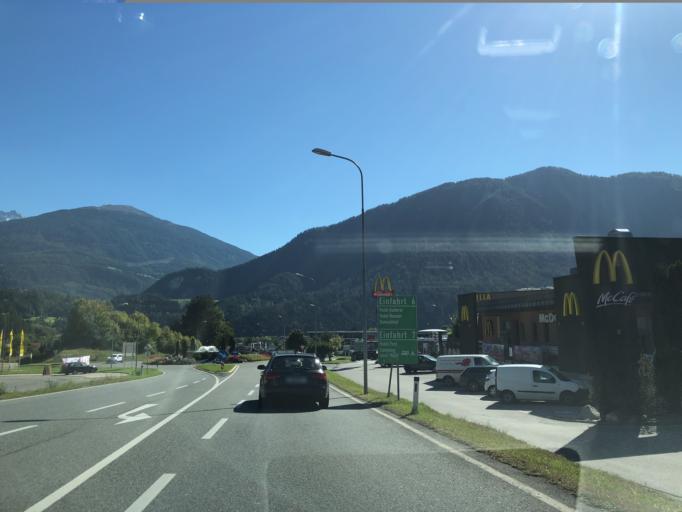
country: AT
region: Tyrol
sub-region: Politischer Bezirk Imst
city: Imst
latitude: 47.2313
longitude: 10.7449
